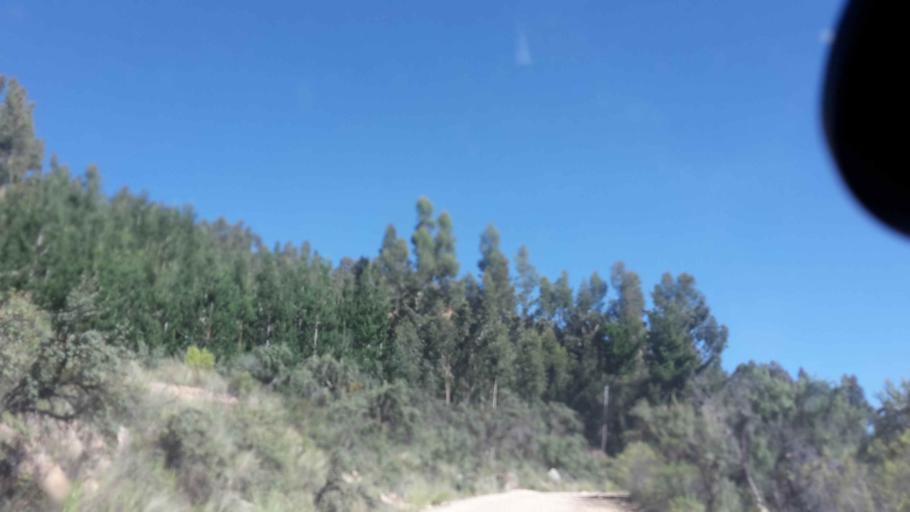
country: BO
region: Cochabamba
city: Arani
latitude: -17.6713
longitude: -65.7290
